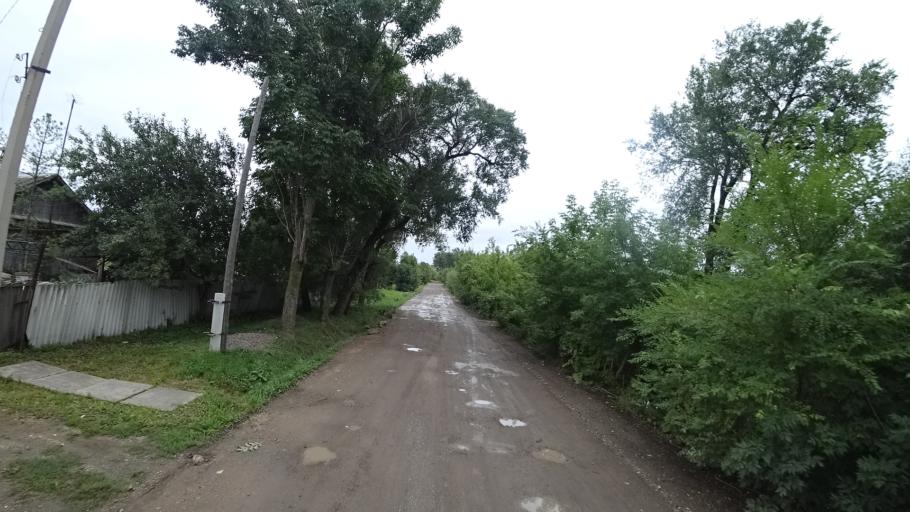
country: RU
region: Primorskiy
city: Chernigovka
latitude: 44.3363
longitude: 132.5608
